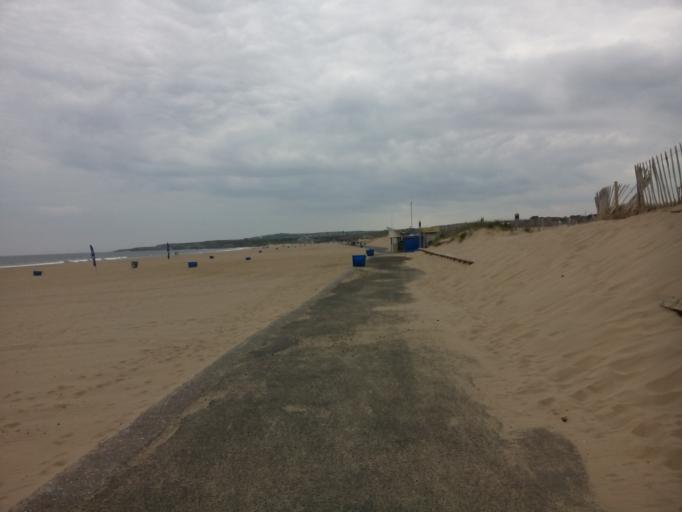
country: GB
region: England
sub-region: South Tyneside
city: South Shields
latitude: 55.0021
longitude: -1.4145
